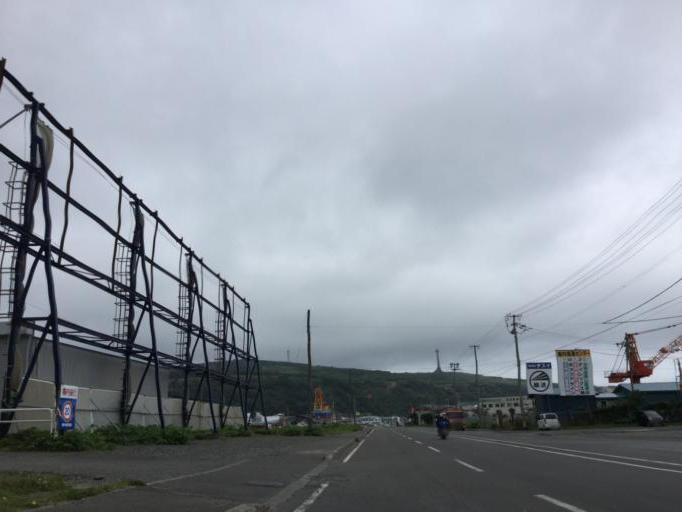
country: JP
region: Hokkaido
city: Wakkanai
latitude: 45.4035
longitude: 141.6837
